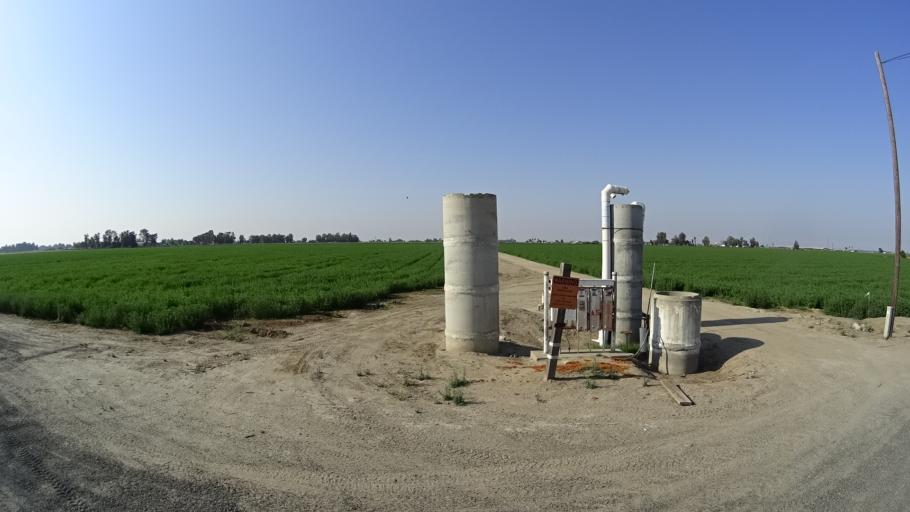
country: US
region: California
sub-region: Fresno County
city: Riverdale
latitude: 36.3585
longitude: -119.8736
